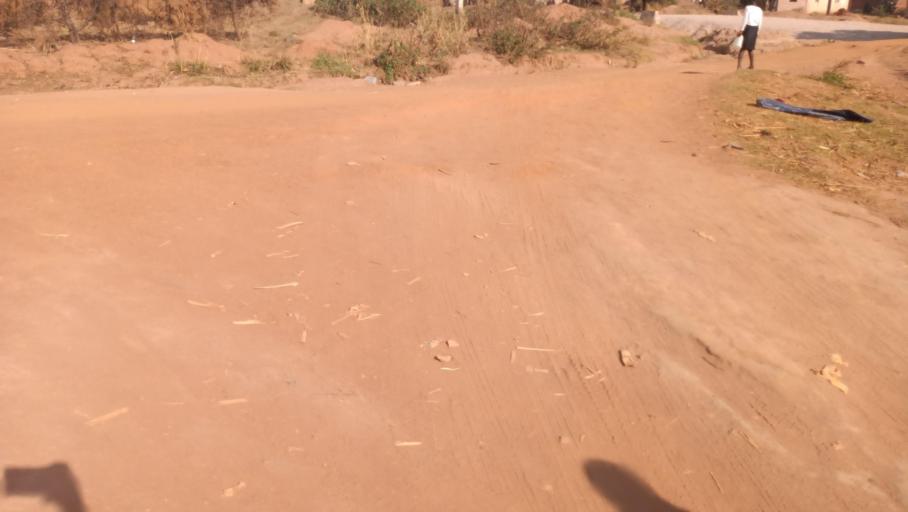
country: ZM
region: Northern
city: Mpika
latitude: -11.8276
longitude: 31.4572
